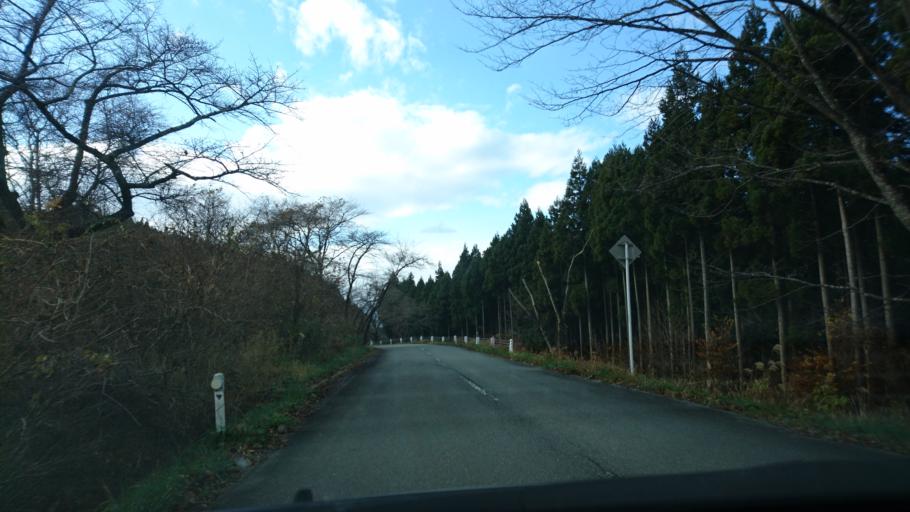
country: JP
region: Iwate
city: Ichinoseki
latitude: 39.0242
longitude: 141.1836
